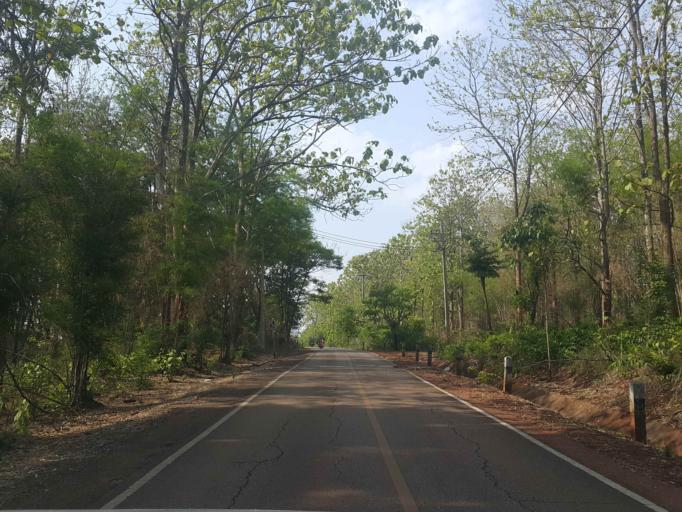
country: TH
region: Chiang Mai
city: Mae Taeng
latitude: 19.0790
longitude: 99.0869
